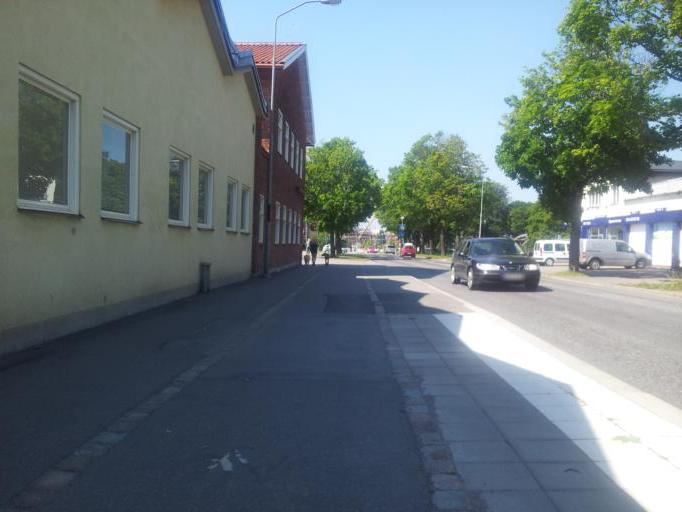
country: SE
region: Uppsala
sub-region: Uppsala Kommun
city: Uppsala
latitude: 59.8566
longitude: 17.6580
